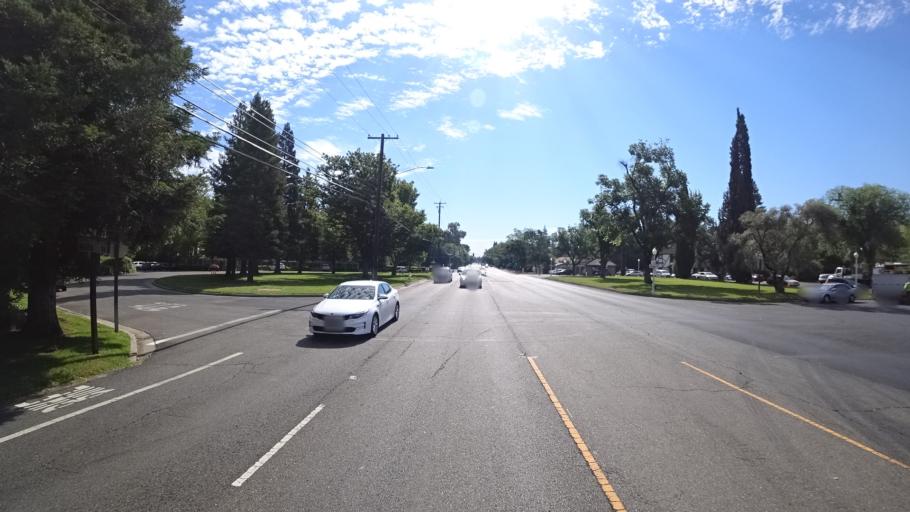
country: US
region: California
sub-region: Sacramento County
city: Arden-Arcade
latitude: 38.5742
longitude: -121.3940
